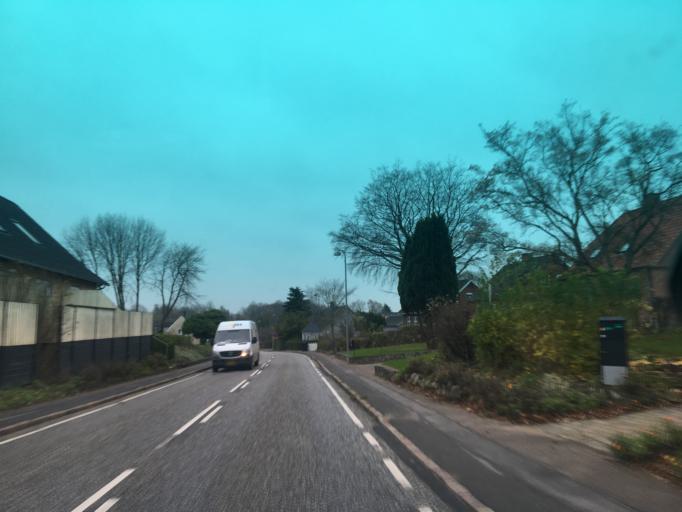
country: DK
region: Zealand
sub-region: Slagelse Kommune
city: Slagelse
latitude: 55.3134
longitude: 11.3961
